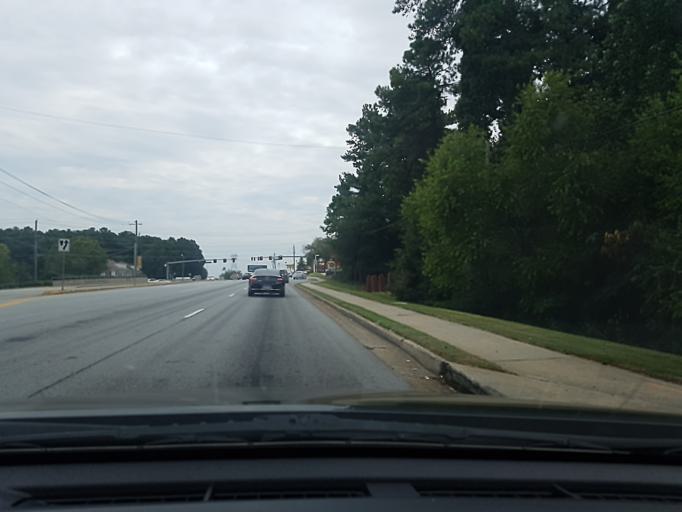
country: US
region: Georgia
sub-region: Gwinnett County
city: Duluth
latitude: 33.9563
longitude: -84.1417
